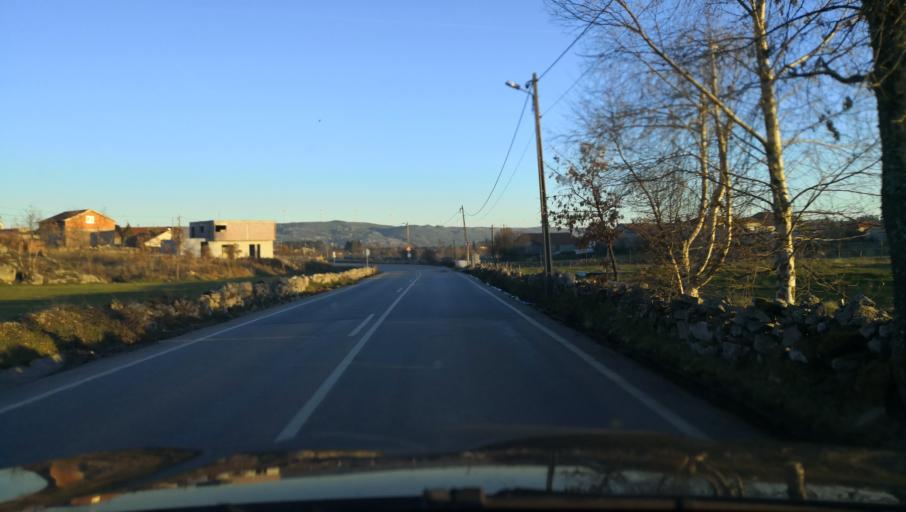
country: PT
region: Vila Real
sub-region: Vila Pouca de Aguiar
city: Vila Pouca de Aguiar
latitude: 41.4979
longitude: -7.6820
